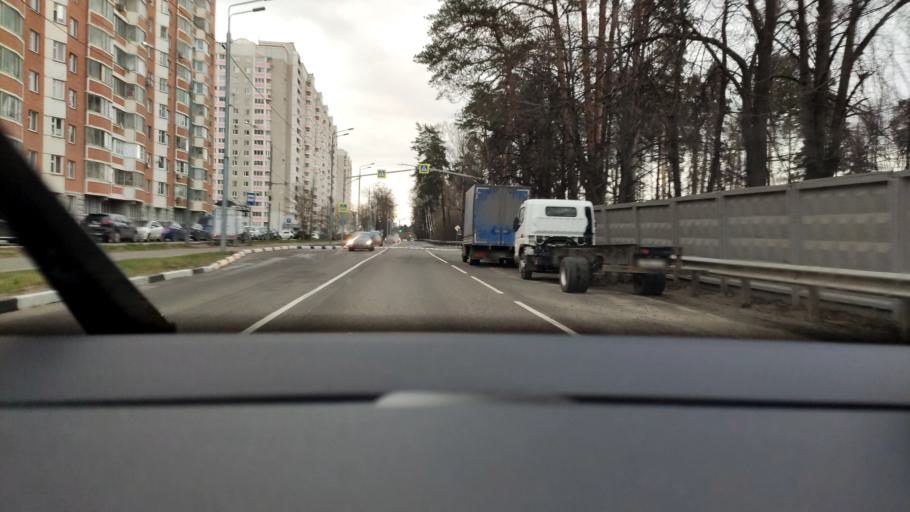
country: RU
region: Moskovskaya
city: Balashikha
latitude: 55.8213
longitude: 37.9421
